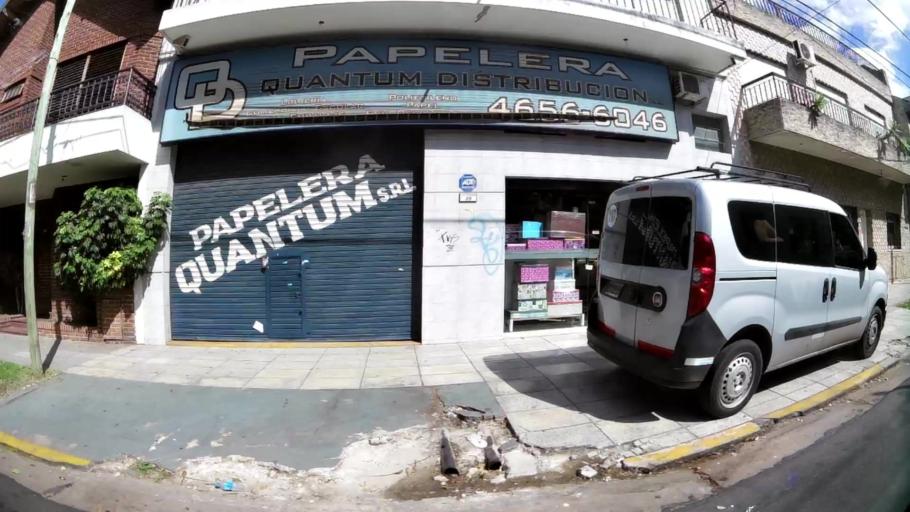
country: AR
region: Buenos Aires
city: San Justo
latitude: -34.6528
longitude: -58.5511
